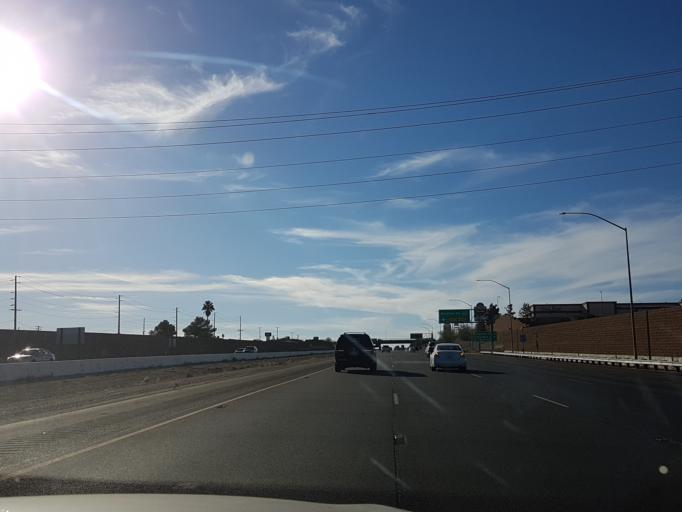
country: US
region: California
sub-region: San Bernardino County
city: Barstow
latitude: 34.8860
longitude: -117.0149
